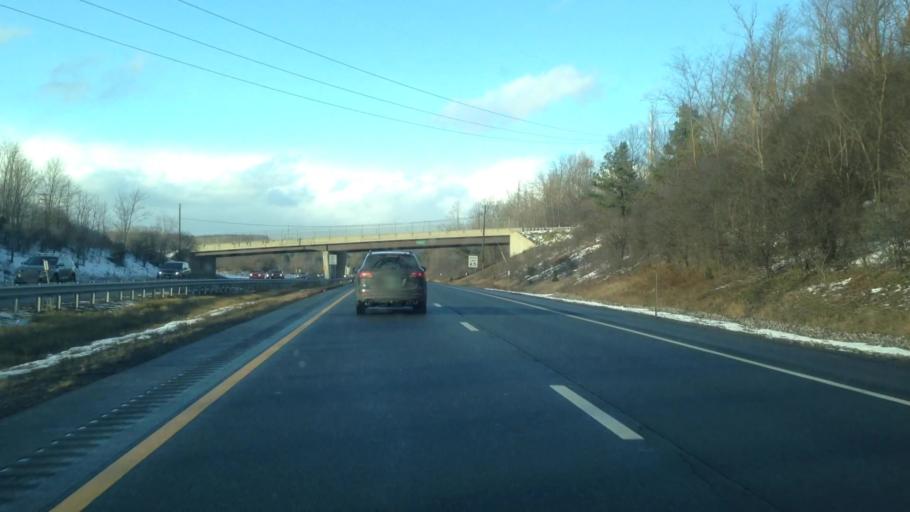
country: US
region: New York
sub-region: Schenectady County
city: Rotterdam
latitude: 42.8045
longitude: -74.0182
